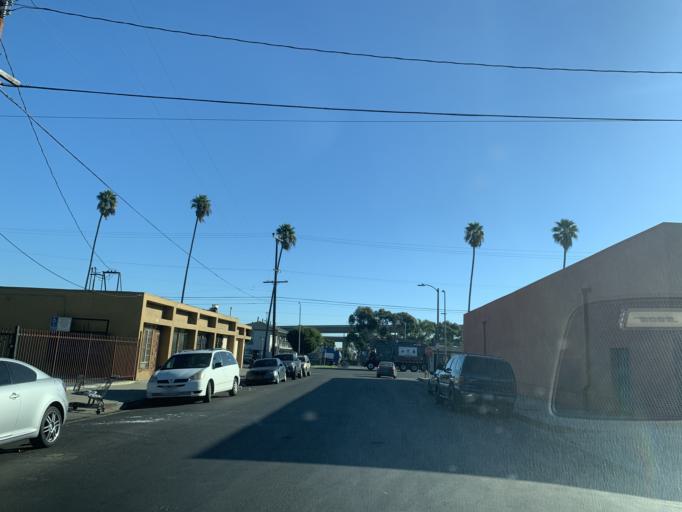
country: US
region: California
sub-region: Los Angeles County
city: Westmont
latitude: 33.9320
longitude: -118.2833
